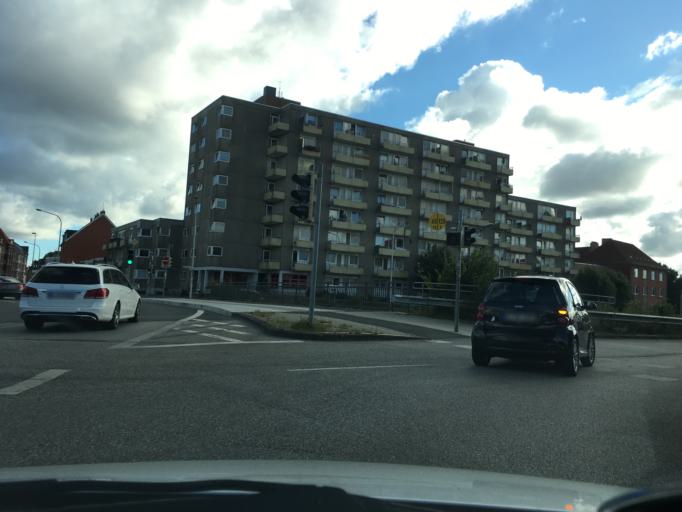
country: DE
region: Schleswig-Holstein
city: Kiel
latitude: 54.3052
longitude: 10.1182
